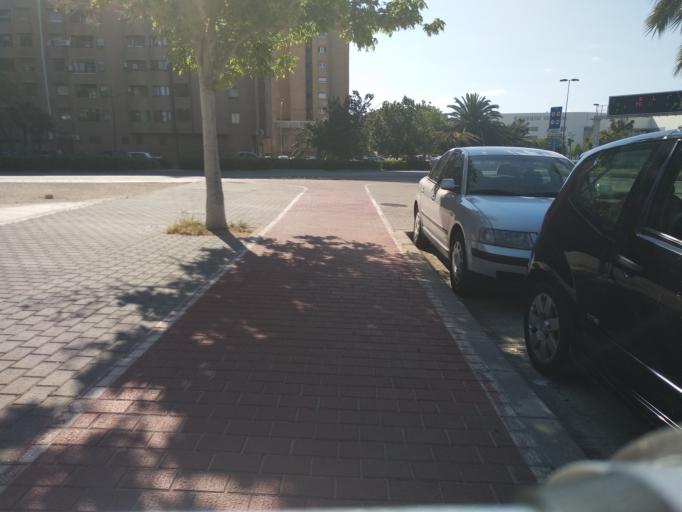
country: ES
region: Valencia
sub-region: Provincia de Valencia
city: Alboraya
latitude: 39.4795
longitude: -0.3510
